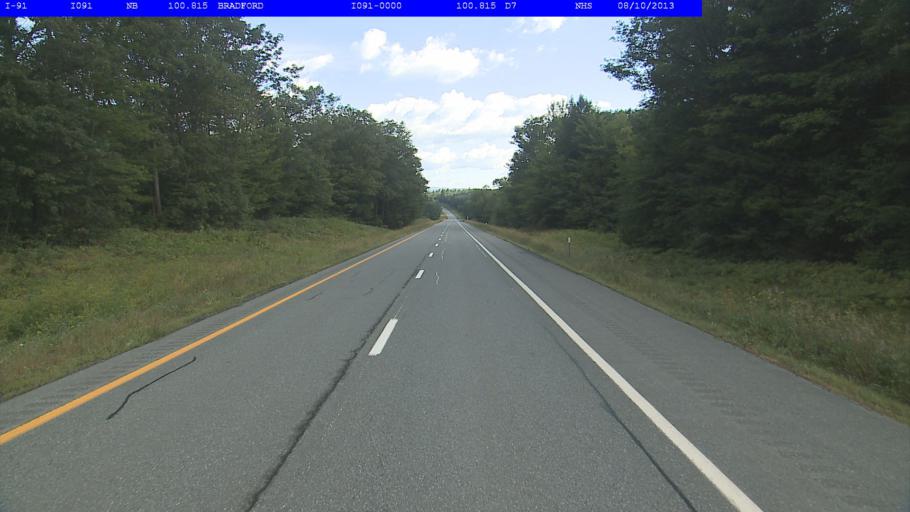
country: US
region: New Hampshire
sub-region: Grafton County
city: Haverhill
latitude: 44.0261
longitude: -72.1151
